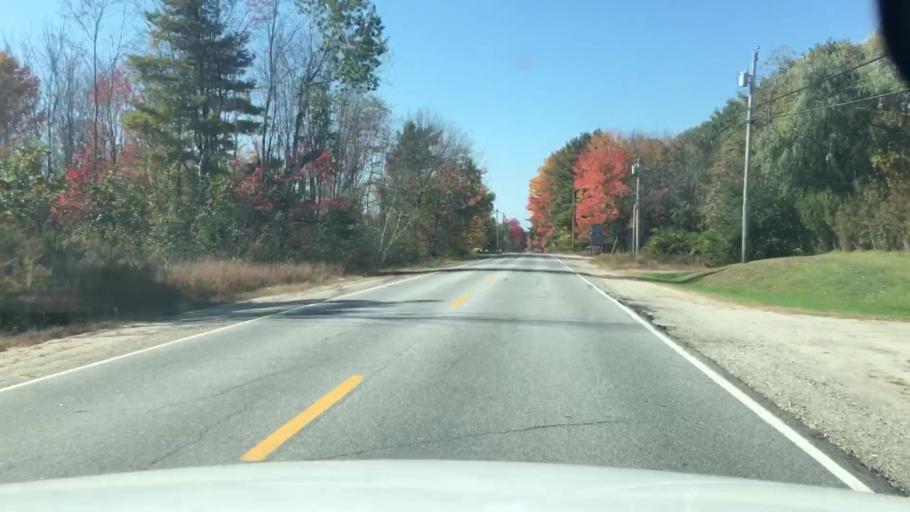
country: US
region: Maine
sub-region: Androscoggin County
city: Lisbon Falls
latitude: 44.0402
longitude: -69.9967
